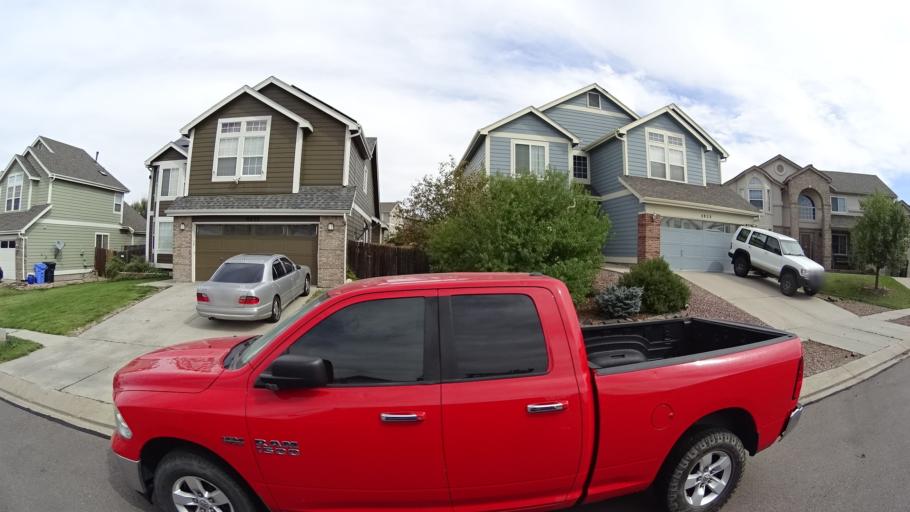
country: US
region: Colorado
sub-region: El Paso County
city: Cimarron Hills
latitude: 38.9034
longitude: -104.6973
